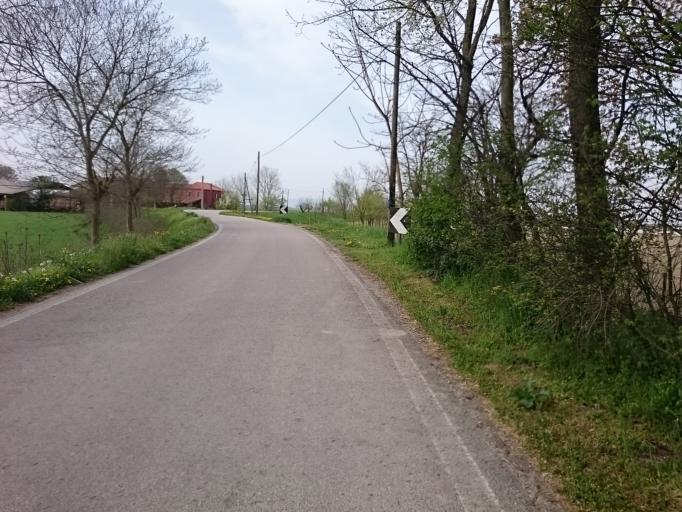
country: IT
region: Veneto
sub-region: Provincia di Padova
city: Anguillara Veneta
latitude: 45.1580
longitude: 11.8517
